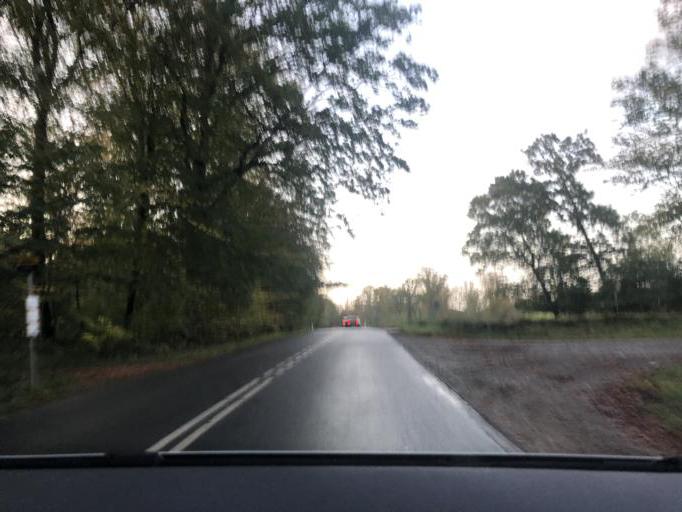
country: DK
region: Capital Region
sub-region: Frederikssund Kommune
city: Slangerup
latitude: 55.8200
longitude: 12.1981
